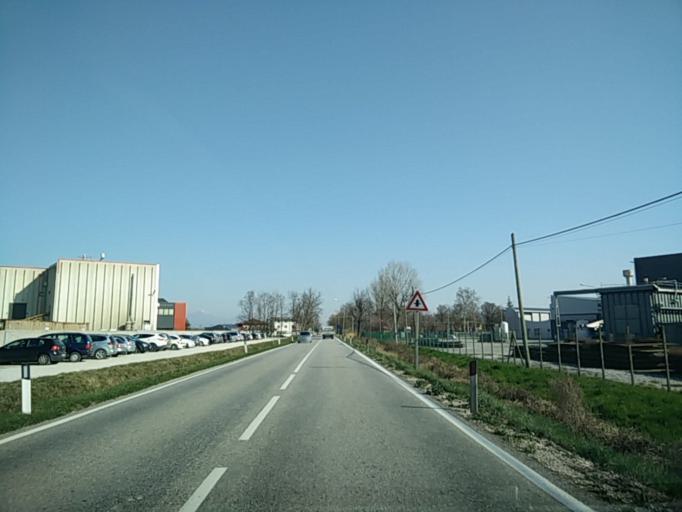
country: IT
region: Friuli Venezia Giulia
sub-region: Provincia di Udine
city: Sedegliano
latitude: 45.9895
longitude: 12.9310
